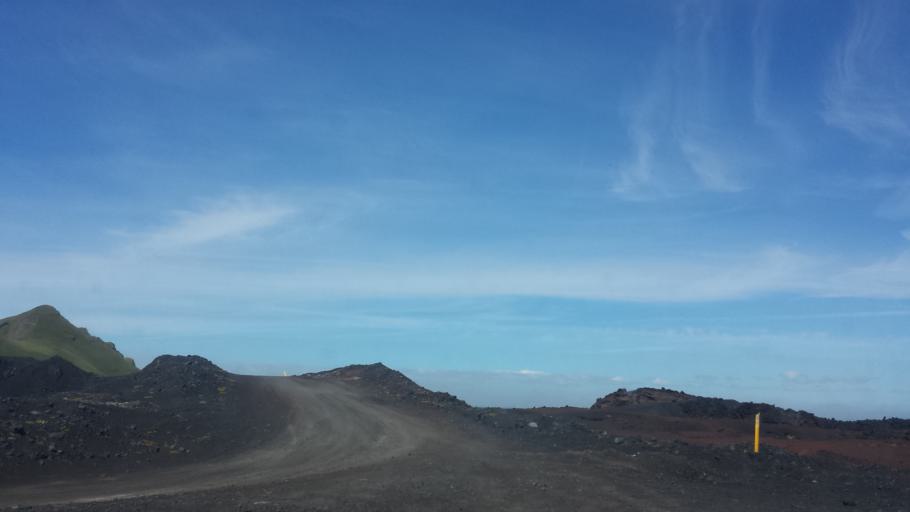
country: IS
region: South
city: Vestmannaeyjar
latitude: 63.4363
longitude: -20.2294
